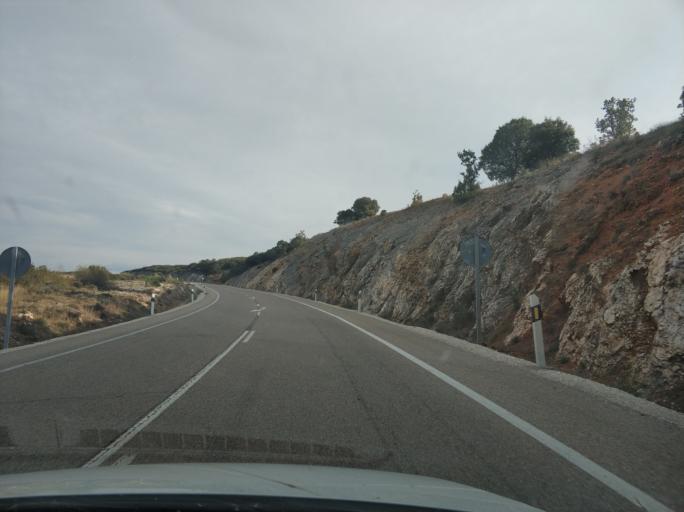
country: ES
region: Castille and Leon
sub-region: Provincia de Burgos
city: Huermeces
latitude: 42.5219
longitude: -3.7282
